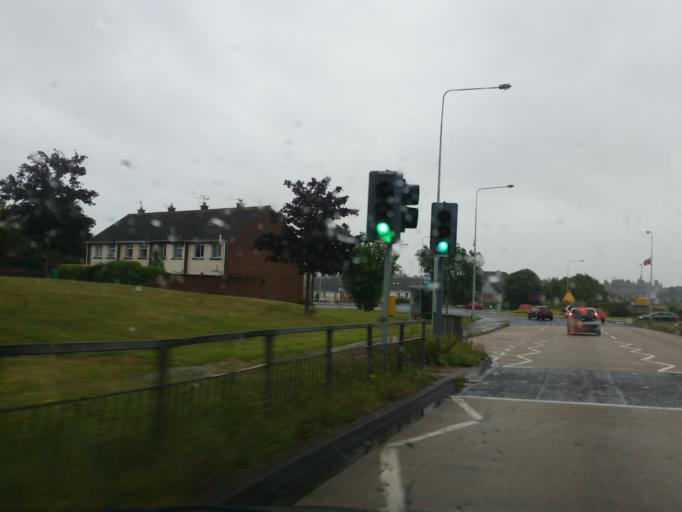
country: GB
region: Northern Ireland
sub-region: North Down District
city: Bangor
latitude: 54.6475
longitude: -5.6616
